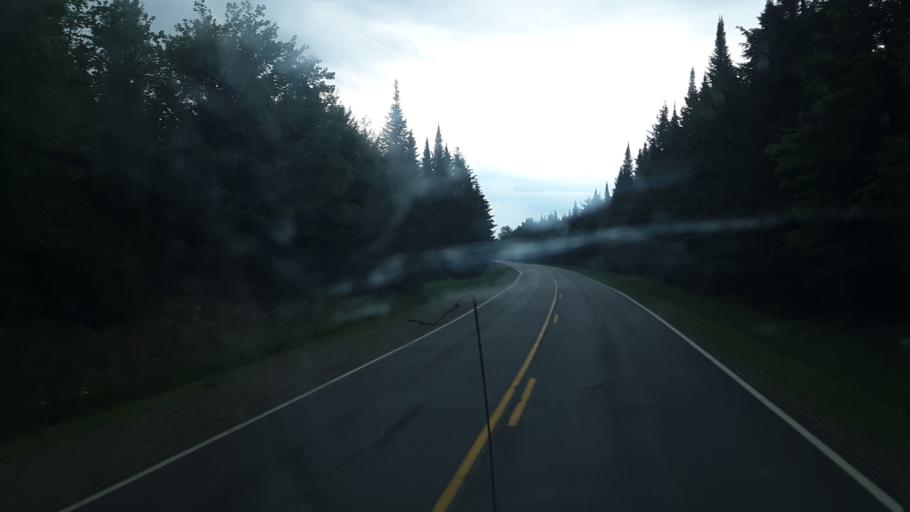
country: US
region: Maine
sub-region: Penobscot County
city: Medway
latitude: 45.6979
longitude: -68.2896
